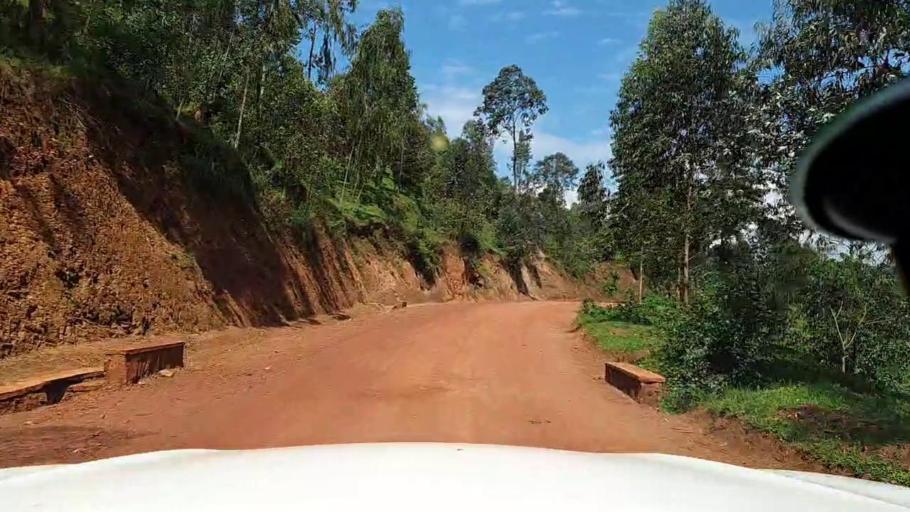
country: RW
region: Kigali
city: Kigali
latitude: -1.7836
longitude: 29.8801
